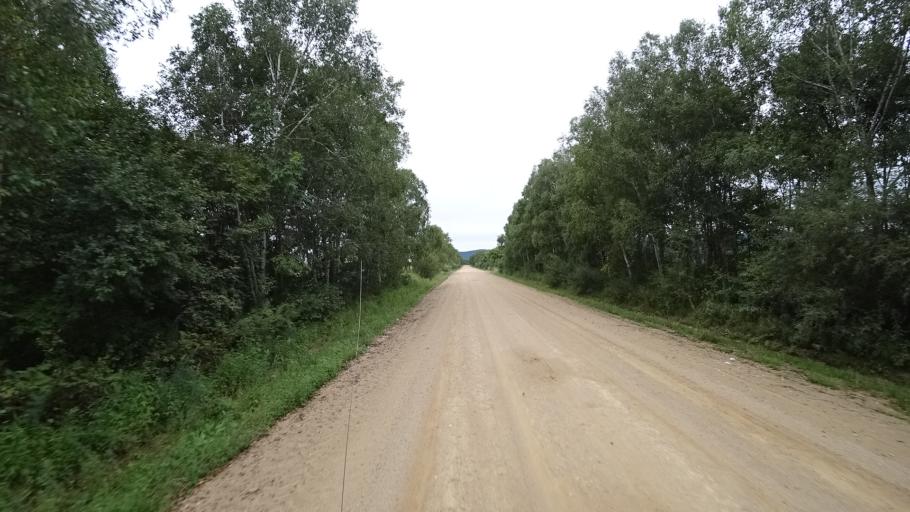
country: RU
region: Primorskiy
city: Rettikhovka
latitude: 44.1595
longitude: 132.6969
